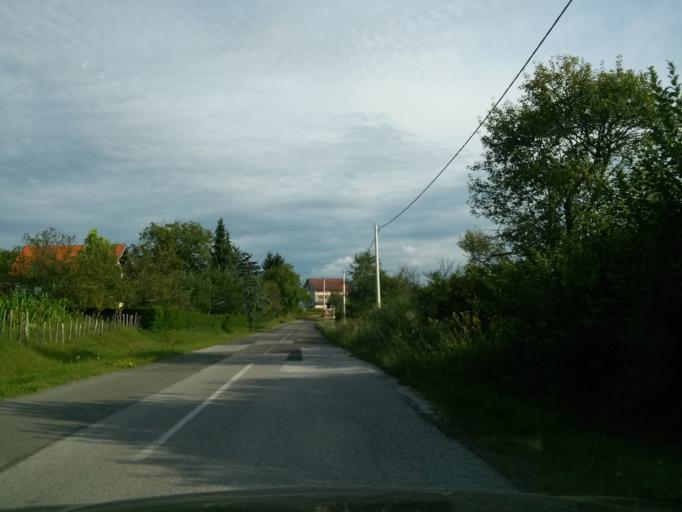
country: HR
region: Sisacko-Moslavacka
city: Gvozd
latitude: 45.4229
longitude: 15.9398
